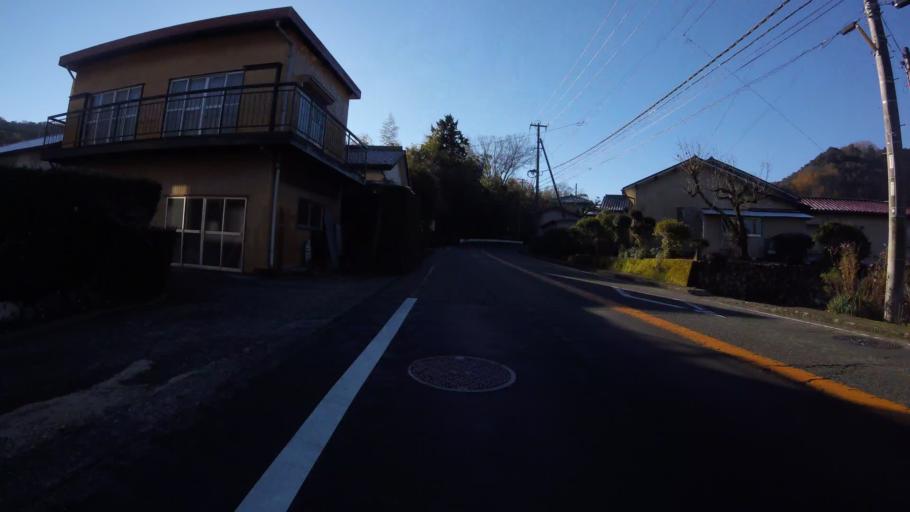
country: JP
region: Shizuoka
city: Heda
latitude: 34.9061
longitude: 138.9245
